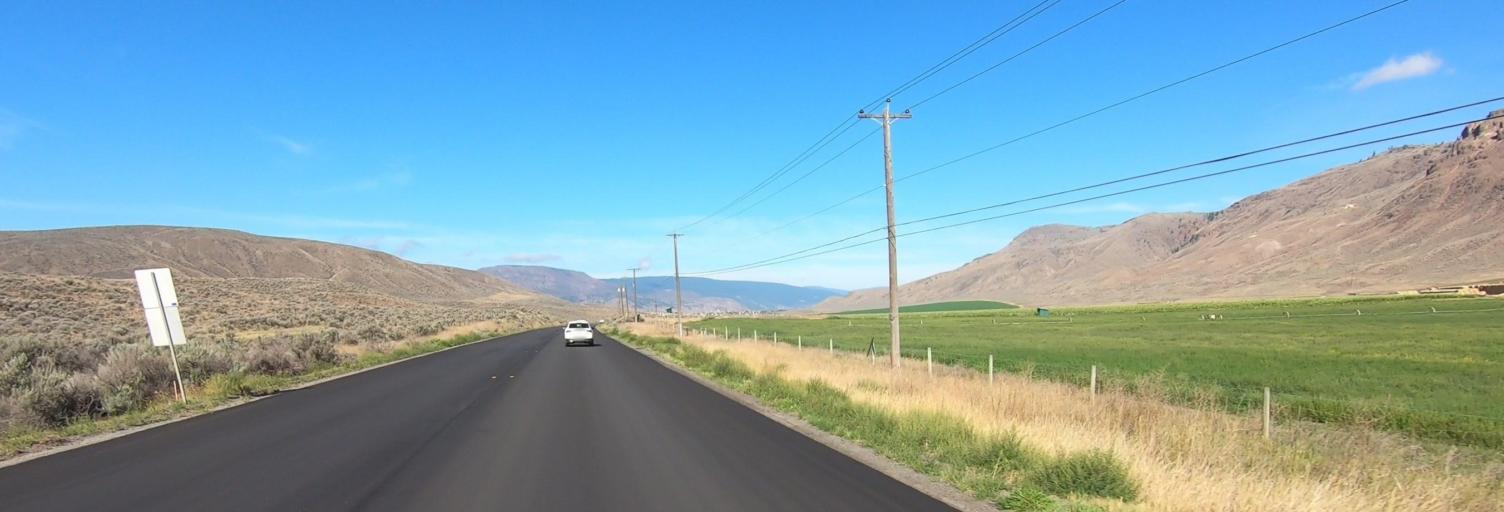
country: CA
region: British Columbia
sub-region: Thompson-Nicola Regional District
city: Ashcroft
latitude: 50.7865
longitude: -121.2165
